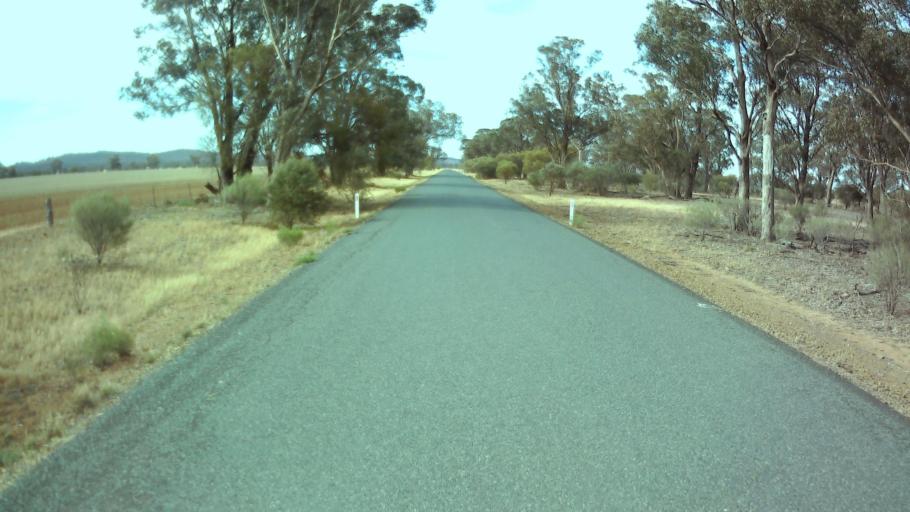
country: AU
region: New South Wales
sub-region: Weddin
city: Grenfell
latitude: -33.8638
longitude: 147.8593
